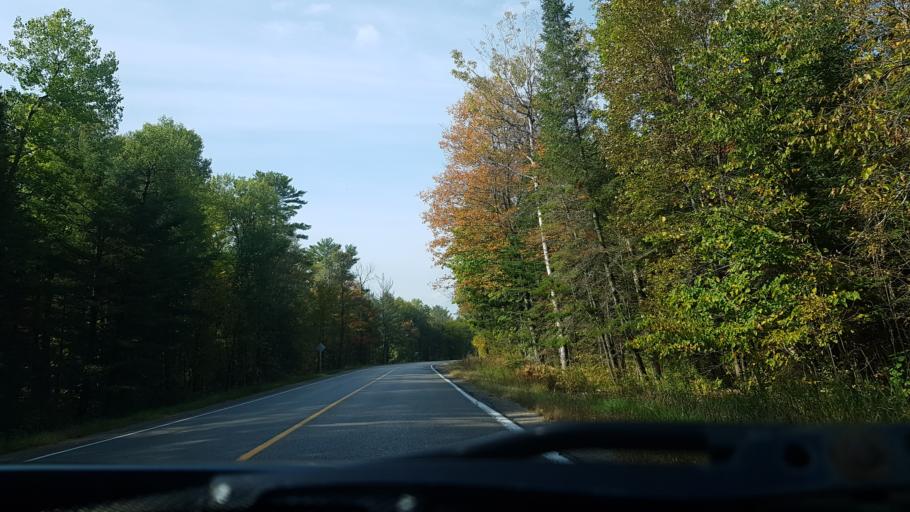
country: CA
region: Ontario
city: Gravenhurst
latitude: 44.7669
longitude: -79.3215
